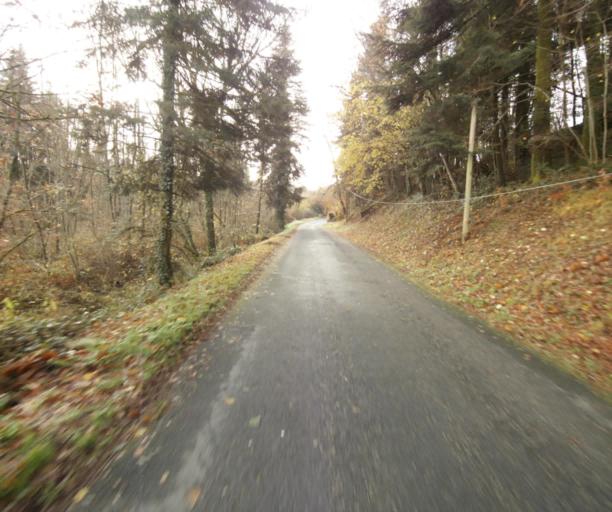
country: FR
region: Limousin
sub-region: Departement de la Correze
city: Cornil
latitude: 45.2147
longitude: 1.7139
